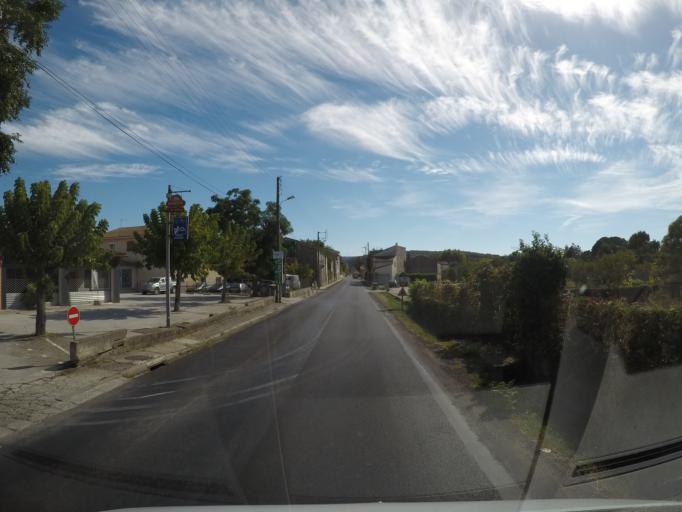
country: FR
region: Languedoc-Roussillon
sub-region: Departement de l'Herault
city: Saint-Bauzille-de-Putois
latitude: 43.8979
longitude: 3.7369
